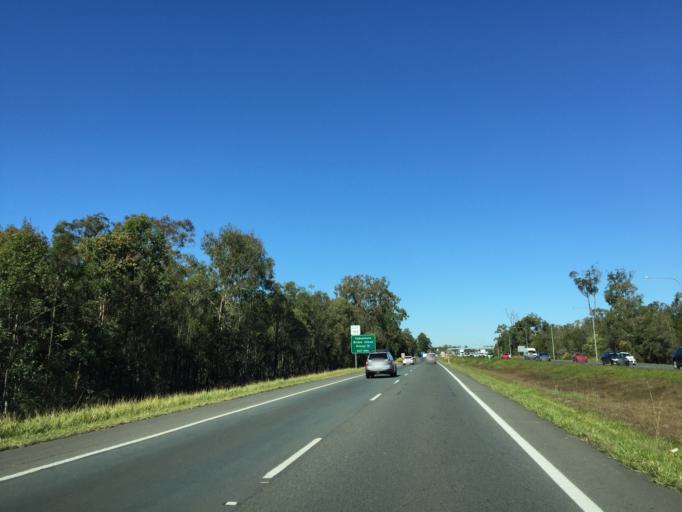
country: AU
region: Queensland
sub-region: Moreton Bay
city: Caboolture
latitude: -27.0618
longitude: 152.9774
